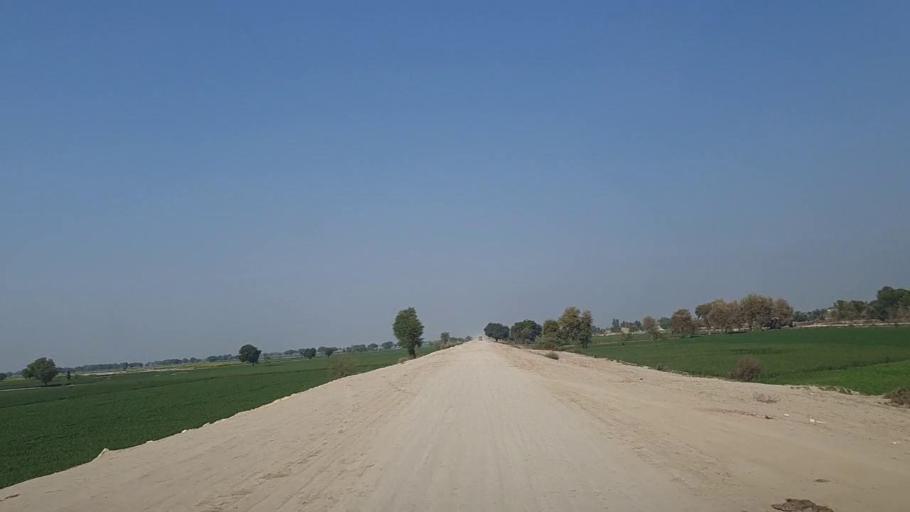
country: PK
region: Sindh
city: Moro
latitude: 26.7334
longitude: 67.9191
